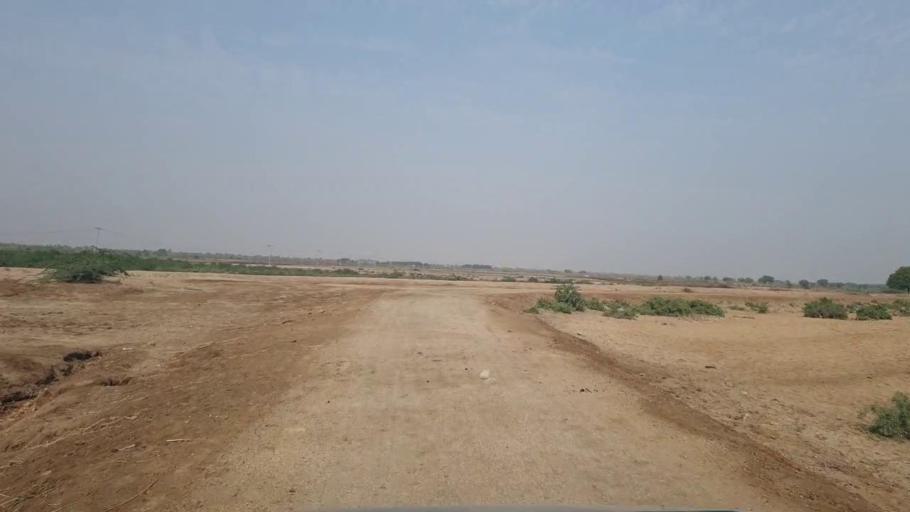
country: PK
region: Sindh
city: Tando Muhammad Khan
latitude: 25.1394
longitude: 68.4563
